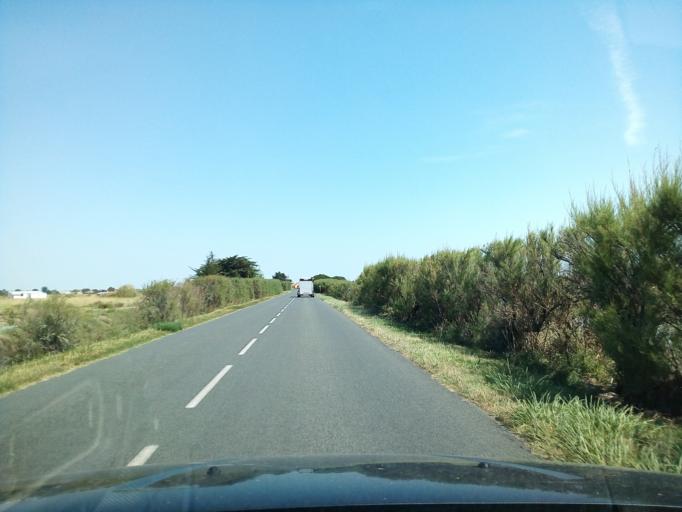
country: FR
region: Poitou-Charentes
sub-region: Departement de la Charente-Maritime
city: Boyard-Ville
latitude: 45.9675
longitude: -1.2639
